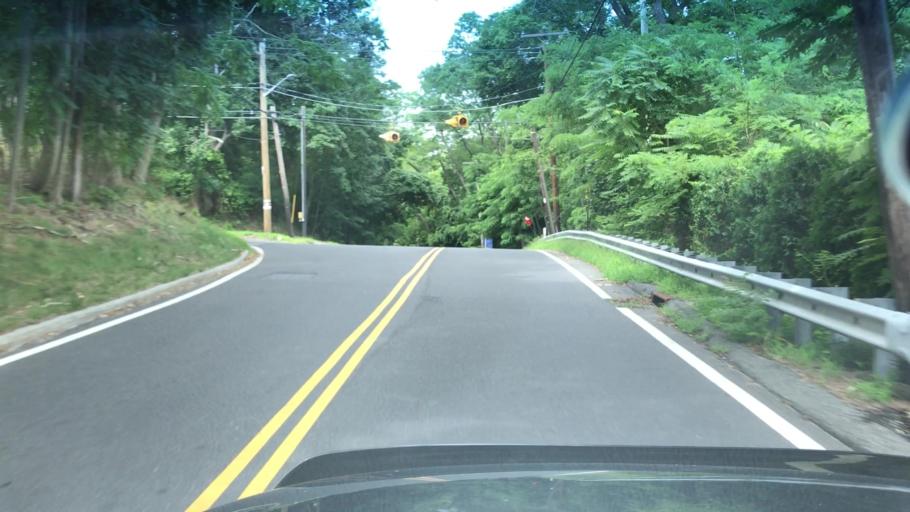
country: US
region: New York
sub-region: Suffolk County
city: Wading River
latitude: 40.9545
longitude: -72.8528
